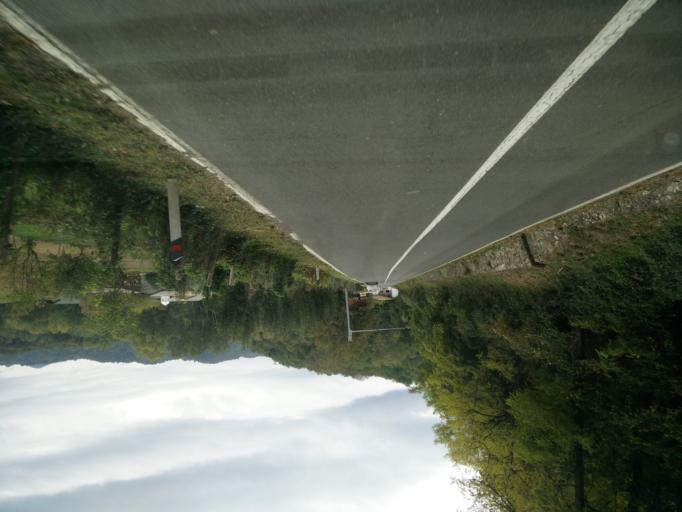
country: IT
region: Tuscany
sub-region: Provincia di Massa-Carrara
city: Fivizzano
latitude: 44.2136
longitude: 10.0923
